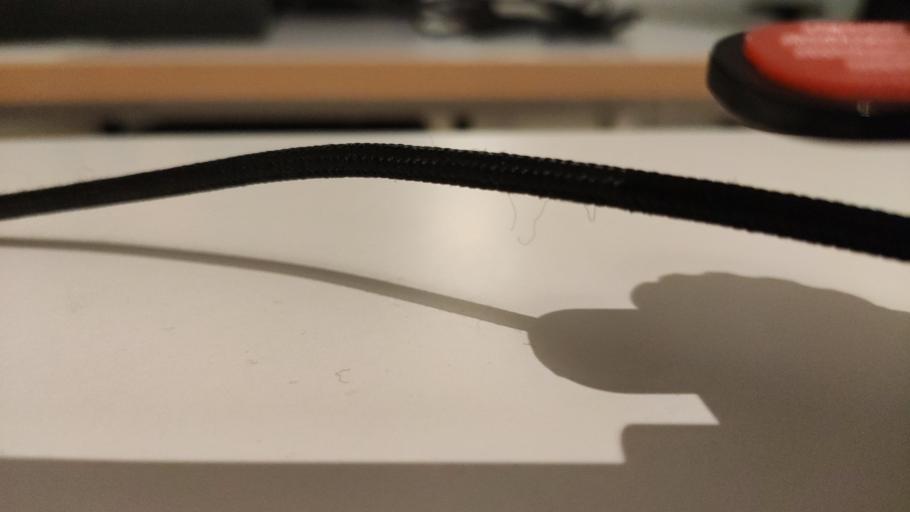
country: RU
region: Moskovskaya
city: Gorshkovo
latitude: 56.3704
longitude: 37.4282
